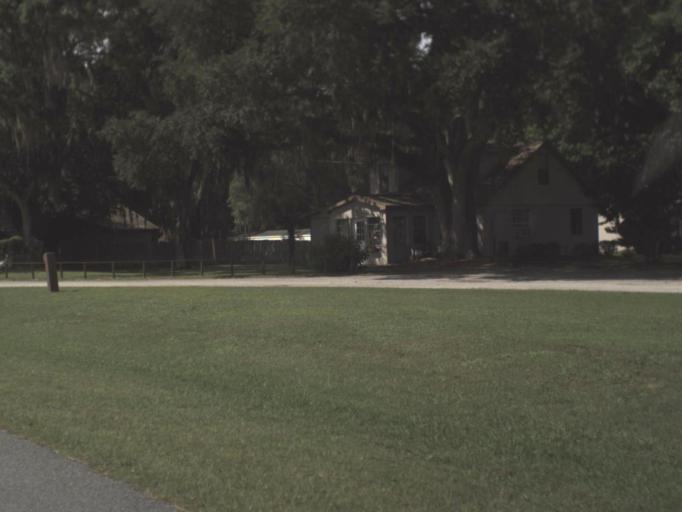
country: US
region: Florida
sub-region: Citrus County
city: Hernando
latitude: 28.9399
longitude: -82.3998
